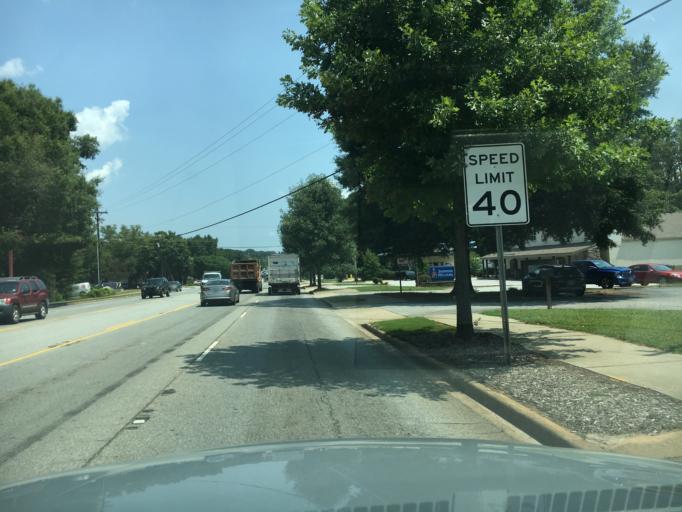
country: US
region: South Carolina
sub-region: Pickens County
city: Clemson
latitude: 34.6923
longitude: -82.8443
